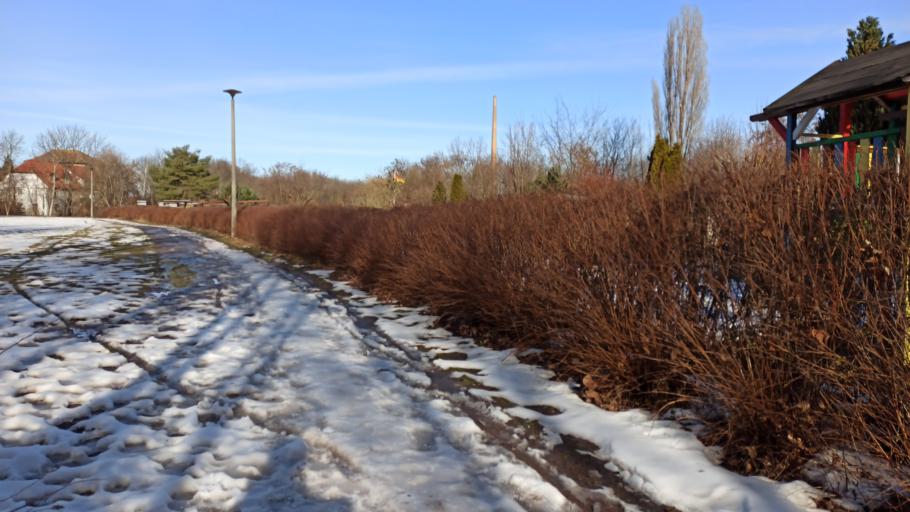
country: DE
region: Thuringia
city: Erfurt
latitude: 51.0175
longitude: 11.0165
